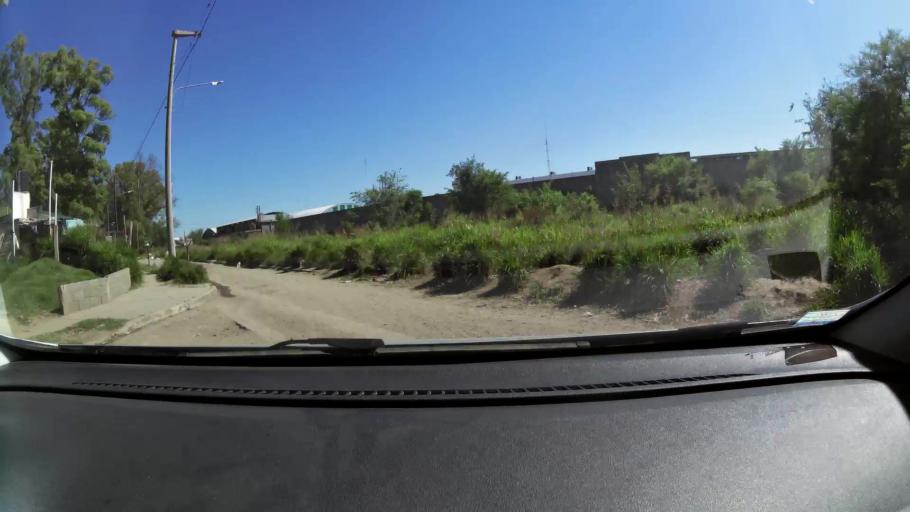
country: AR
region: Cordoba
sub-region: Departamento de Capital
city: Cordoba
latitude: -31.4376
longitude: -64.1320
